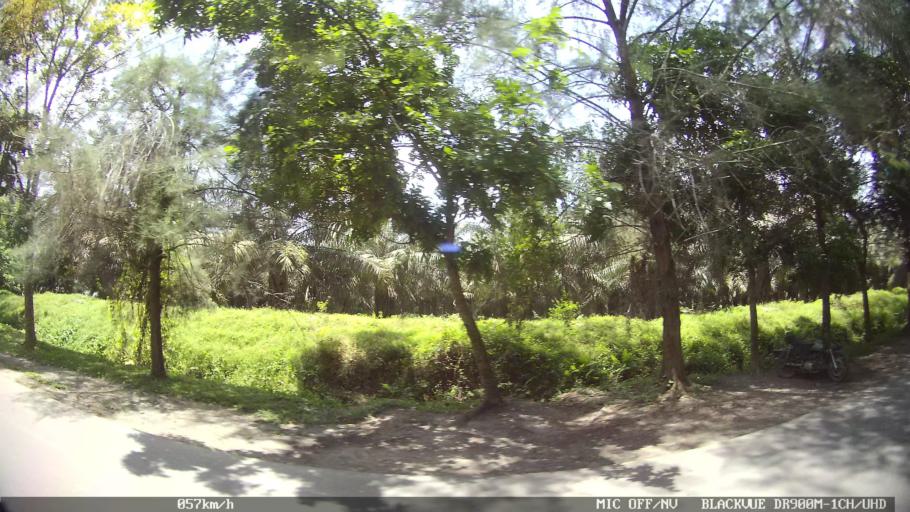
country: ID
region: North Sumatra
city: Percut
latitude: 3.5435
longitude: 98.8695
